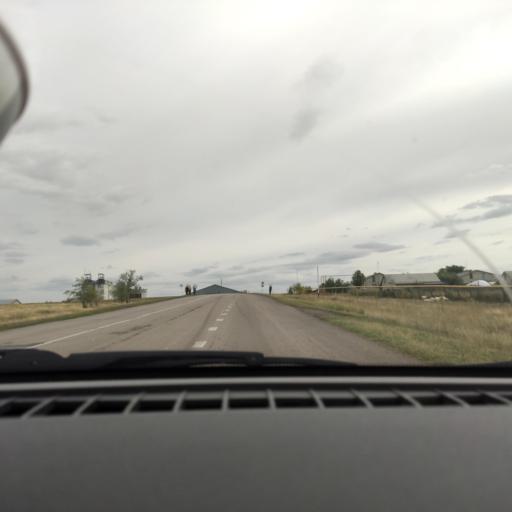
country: RU
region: Samara
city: Georgiyevka
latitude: 53.4745
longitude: 50.9343
